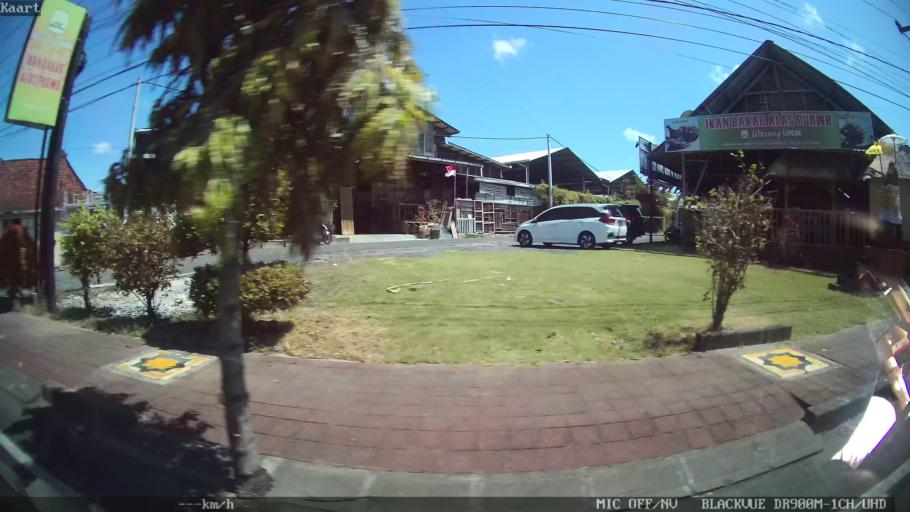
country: ID
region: Bali
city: Denpasar
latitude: -8.6573
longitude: 115.1746
